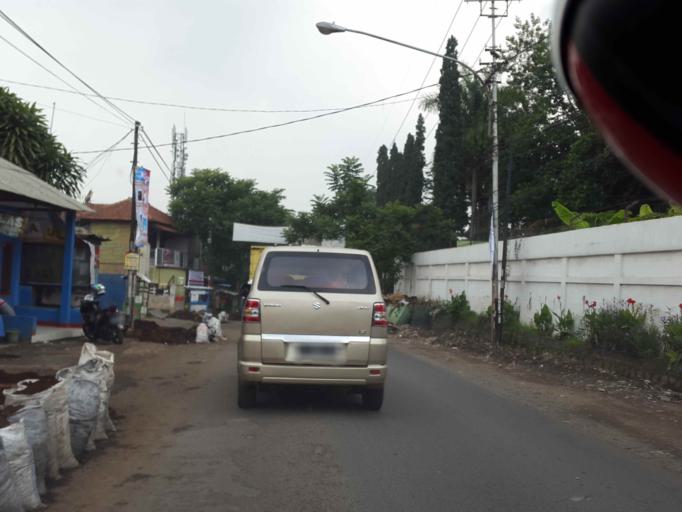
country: ID
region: West Java
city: Cimahi
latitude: -6.8997
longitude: 107.5496
